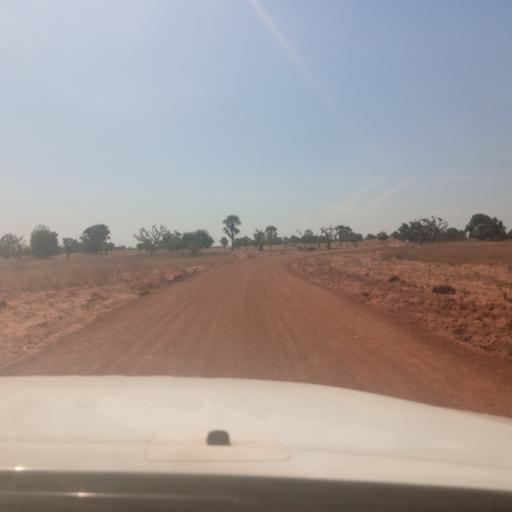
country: NG
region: Adamawa
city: Yola
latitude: 9.1933
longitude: 12.8730
